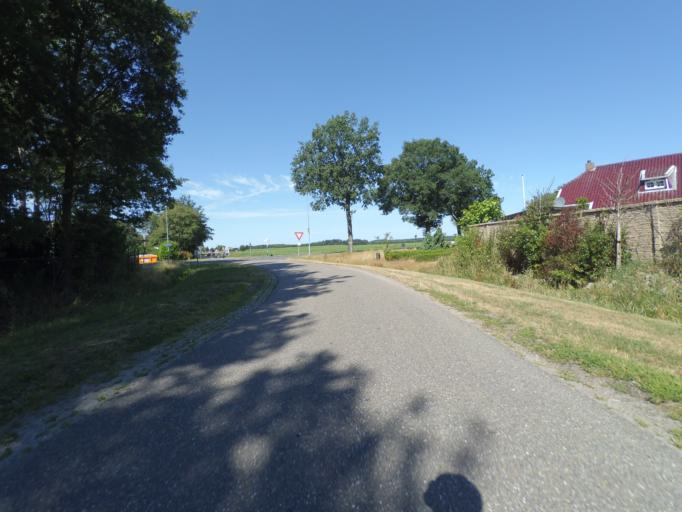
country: NL
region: Drenthe
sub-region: Gemeente Aa en Hunze
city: Anloo
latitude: 52.9496
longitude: 6.6678
